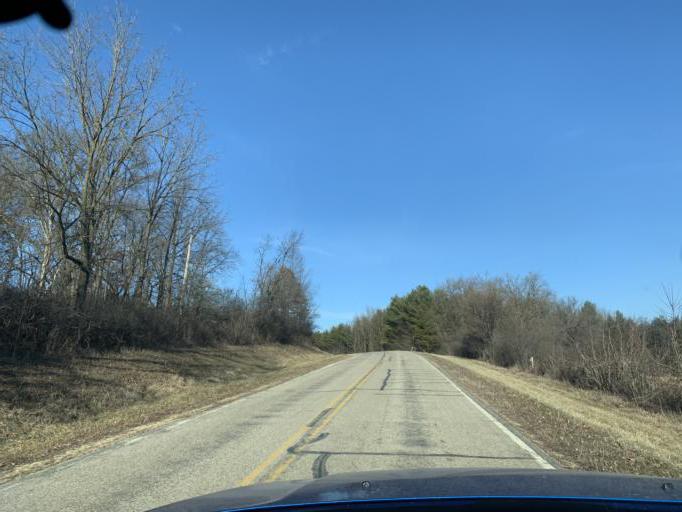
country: US
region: Wisconsin
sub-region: Iowa County
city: Barneveld
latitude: 42.8414
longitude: -89.9309
